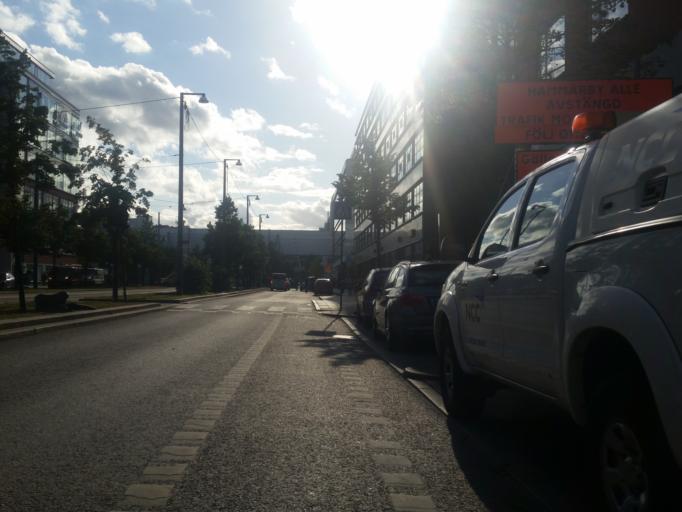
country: SE
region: Stockholm
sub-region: Stockholms Kommun
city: OEstermalm
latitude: 59.3034
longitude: 18.0906
